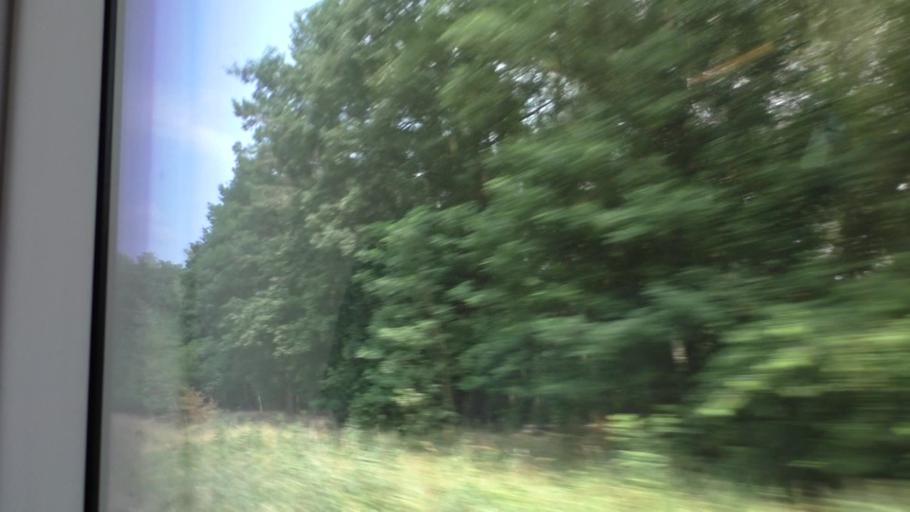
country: DE
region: Brandenburg
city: Mullrose
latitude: 52.2358
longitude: 14.4318
